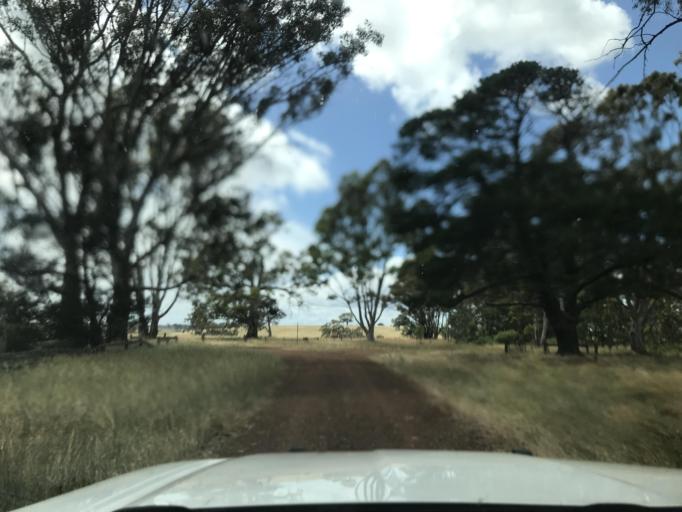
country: AU
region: South Australia
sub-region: Wattle Range
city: Penola
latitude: -37.1855
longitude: 141.4847
